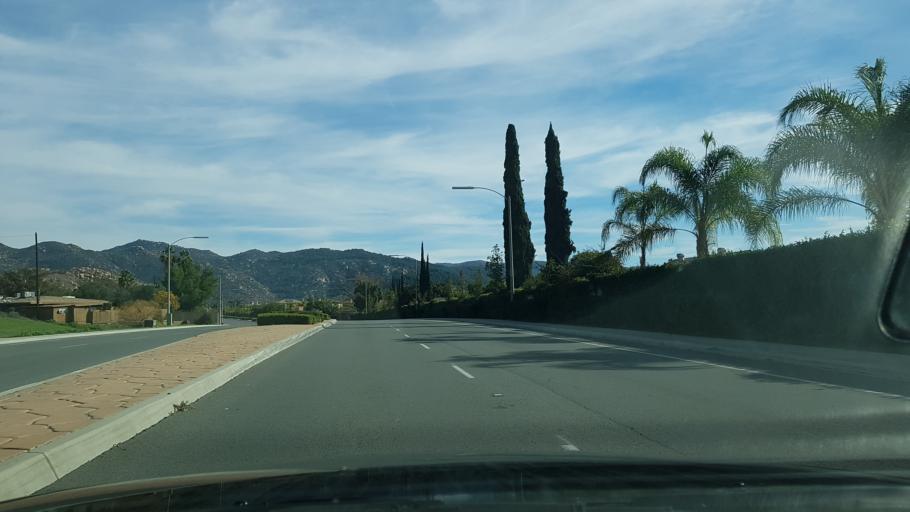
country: US
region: California
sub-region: San Diego County
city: Escondido
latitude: 33.1495
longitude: -117.0504
